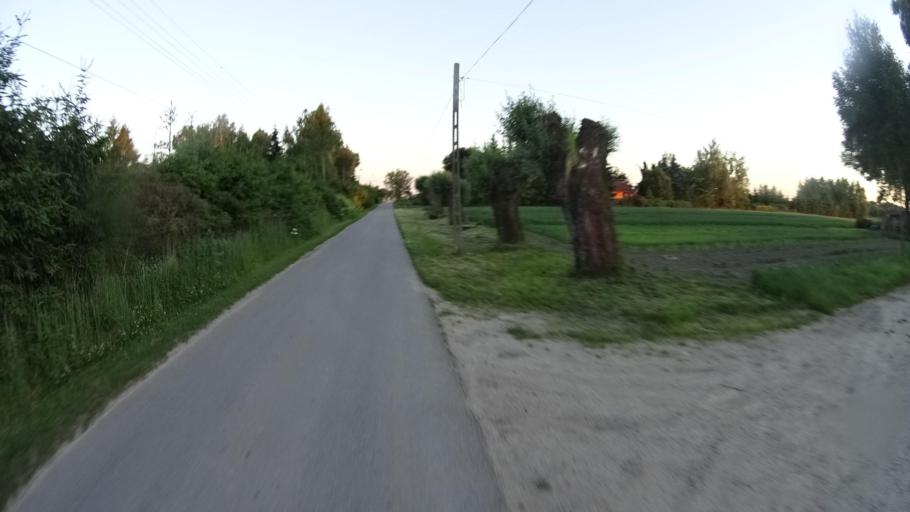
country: PL
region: Masovian Voivodeship
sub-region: Powiat warszawski zachodni
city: Jozefow
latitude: 52.2439
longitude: 20.6594
